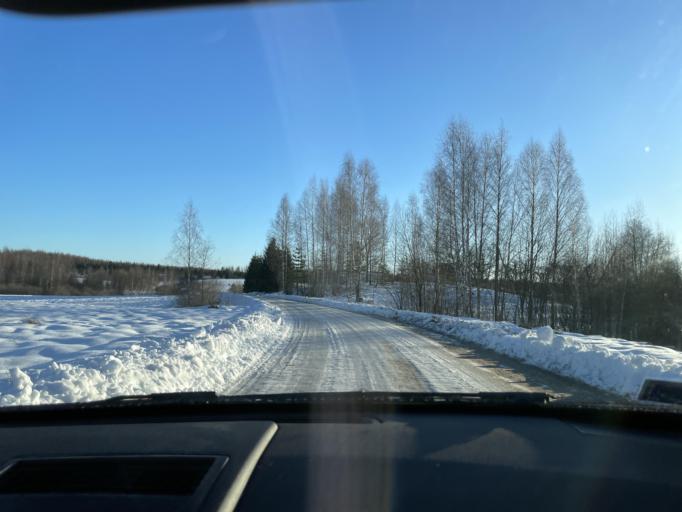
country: LV
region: Ludzas Rajons
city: Ludza
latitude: 56.4611
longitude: 27.6090
